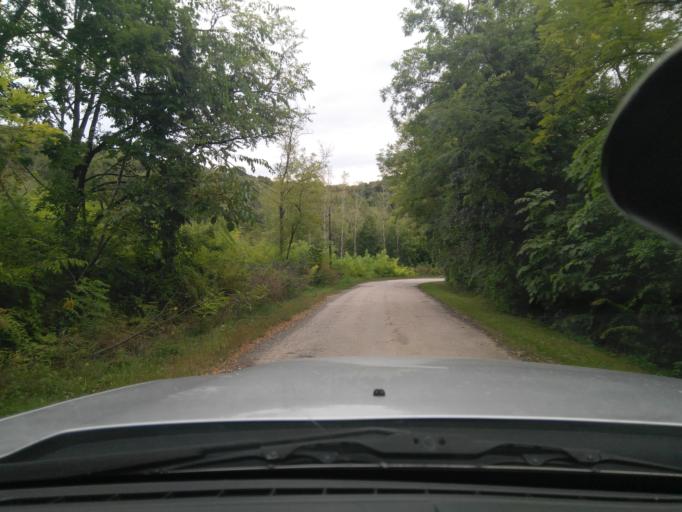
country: HU
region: Fejer
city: Val
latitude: 47.3737
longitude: 18.6828
